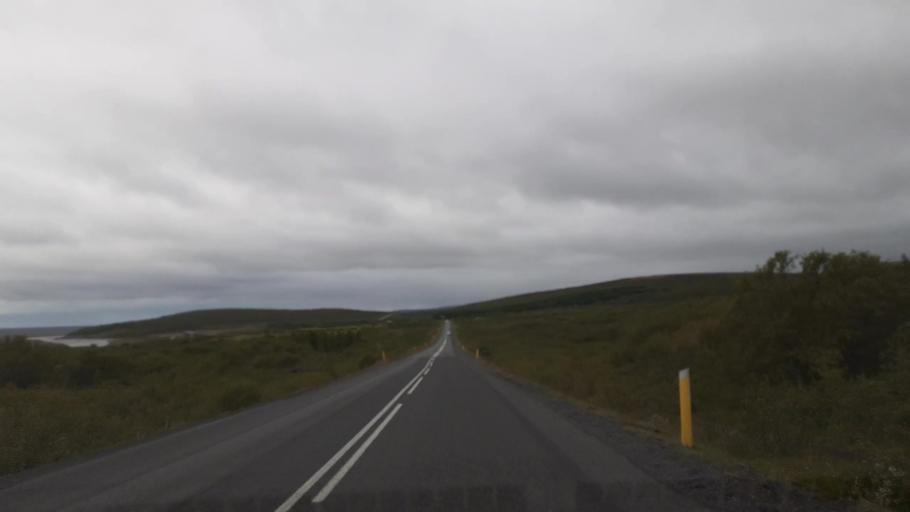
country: IS
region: Northeast
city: Husavik
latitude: 66.0370
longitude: -16.4383
